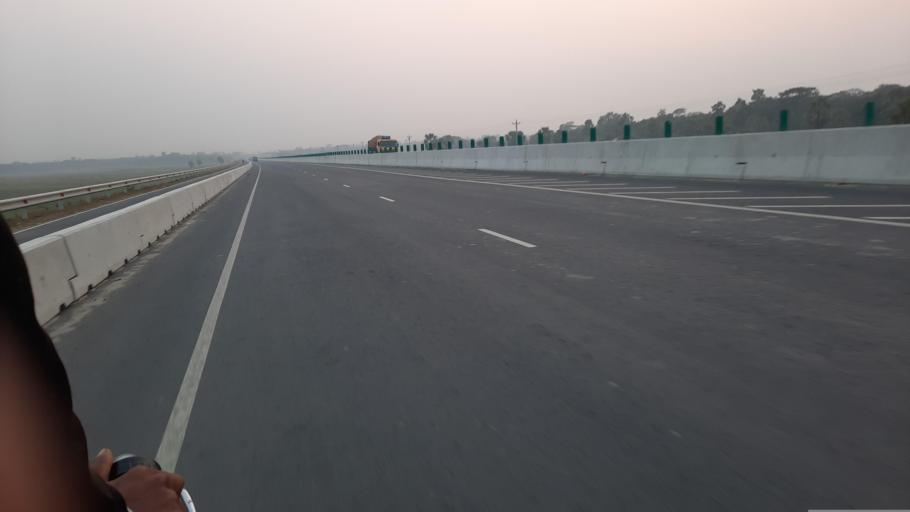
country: BD
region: Khulna
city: Kalia
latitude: 23.2056
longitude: 89.7098
